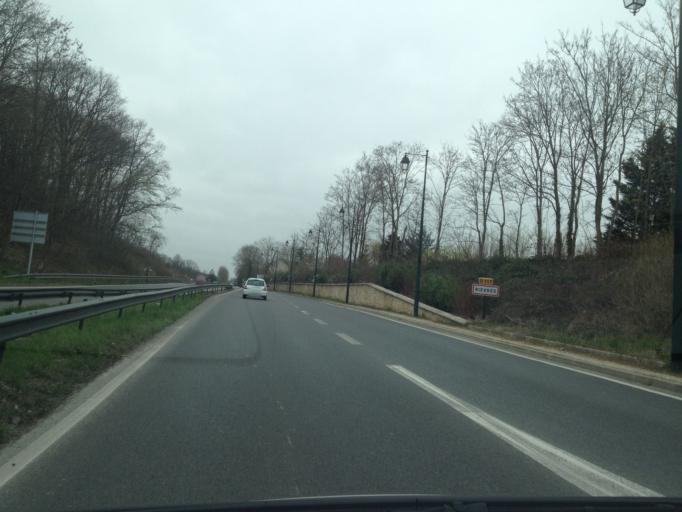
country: FR
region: Ile-de-France
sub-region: Departement de l'Essonne
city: Igny
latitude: 48.7489
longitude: 2.2166
